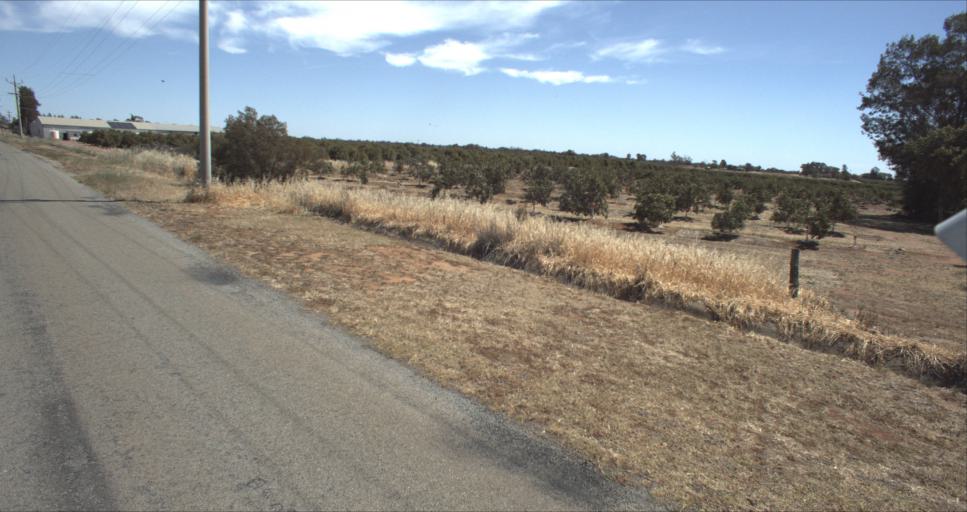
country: AU
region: New South Wales
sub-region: Leeton
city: Leeton
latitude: -34.5968
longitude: 146.4376
